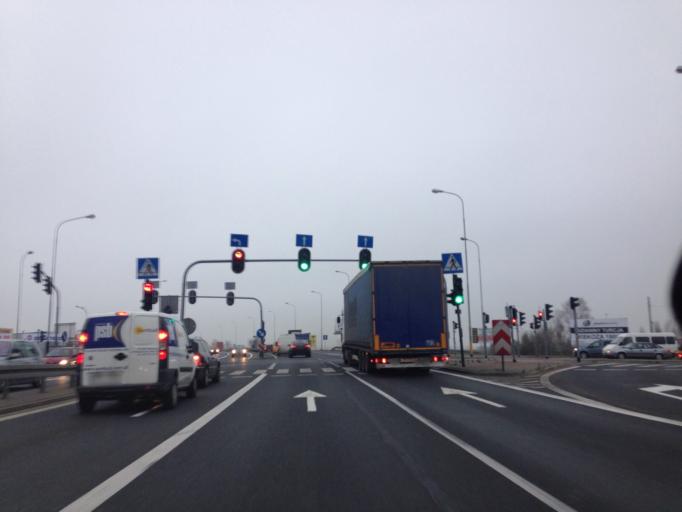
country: PL
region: Lodz Voivodeship
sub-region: Powiat lodzki wschodni
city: Rzgow
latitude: 51.6613
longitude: 19.4765
